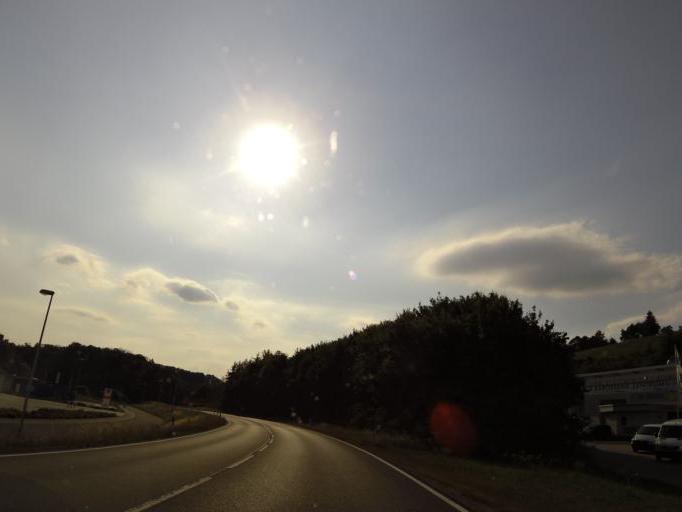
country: DE
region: Bavaria
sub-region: Regierungsbezirk Unterfranken
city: Marktheidenfeld
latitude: 49.8285
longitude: 9.6182
